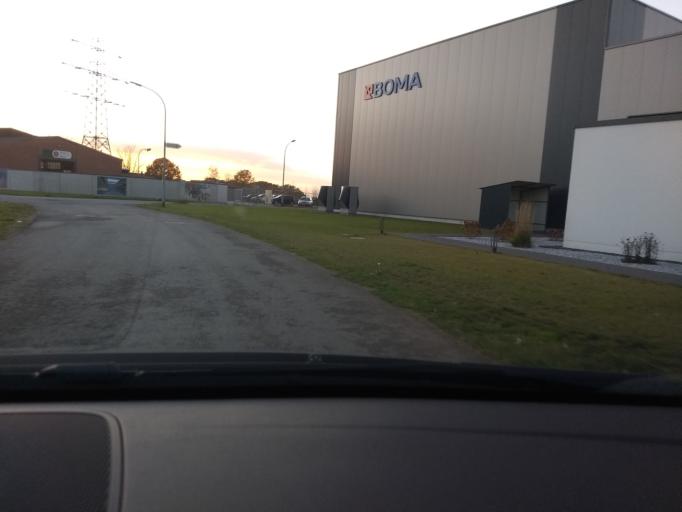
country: DE
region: North Rhine-Westphalia
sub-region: Regierungsbezirk Munster
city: Borken
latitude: 51.8521
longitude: 6.8925
